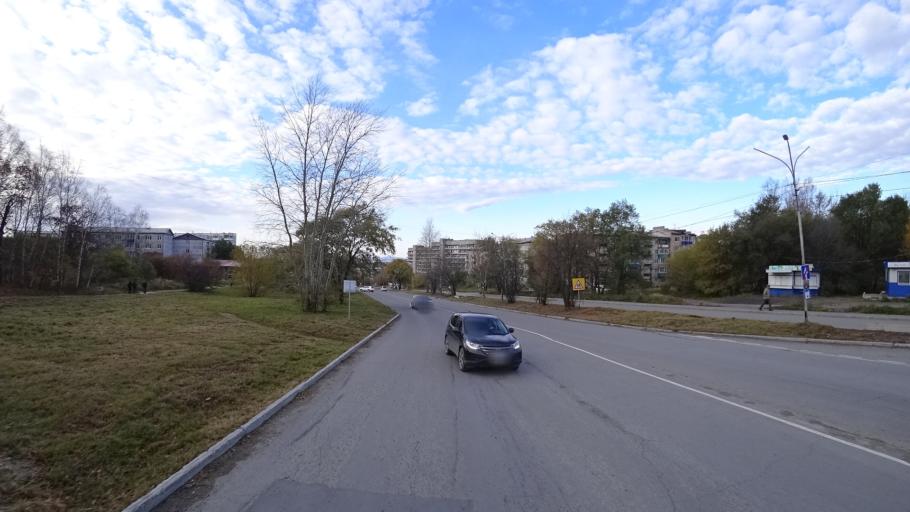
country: RU
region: Khabarovsk Krai
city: Amursk
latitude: 50.2416
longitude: 136.9134
